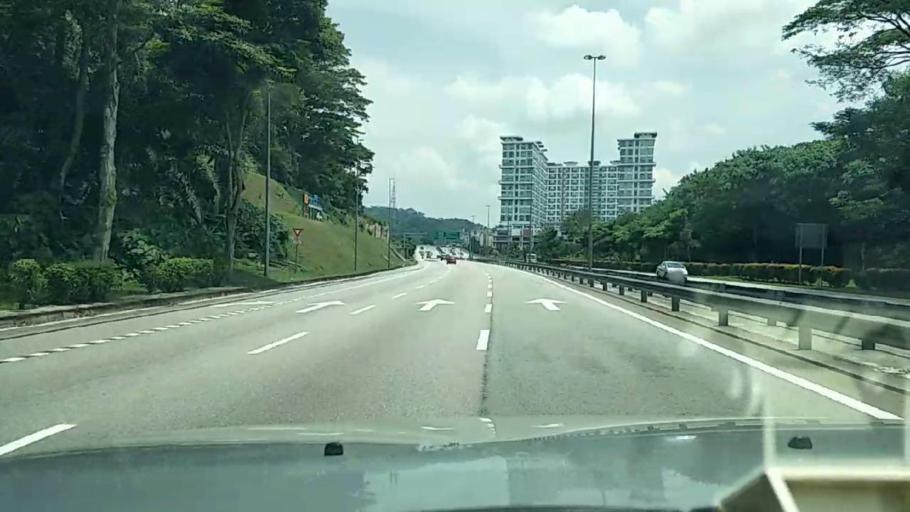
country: MY
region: Kuala Lumpur
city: Kuala Lumpur
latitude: 3.0942
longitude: 101.6798
